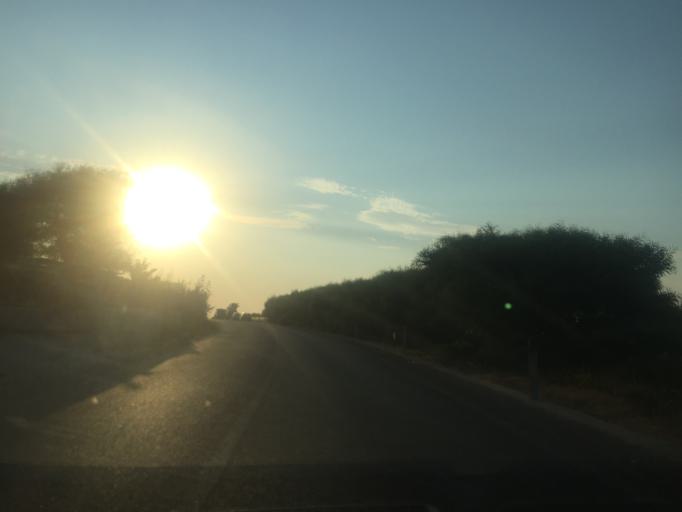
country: IT
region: Sicily
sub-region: Ragusa
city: Cava d'Aliga
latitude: 36.7141
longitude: 14.7614
